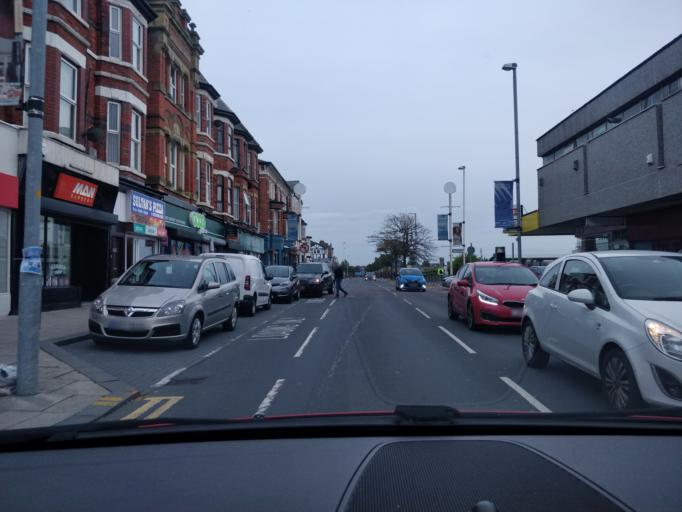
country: GB
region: England
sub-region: Sefton
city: Southport
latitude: 53.6475
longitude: -3.0024
